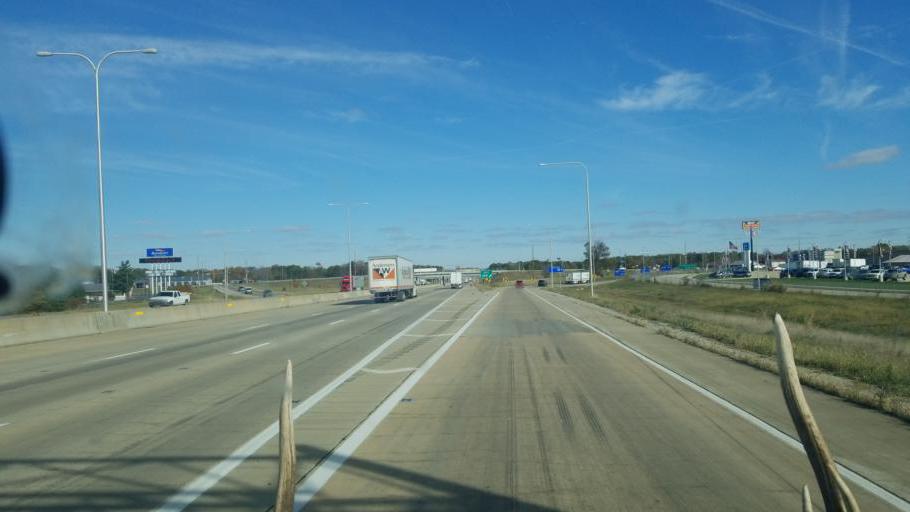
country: US
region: Illinois
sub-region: Effingham County
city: Effingham
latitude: 39.1165
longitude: -88.5695
